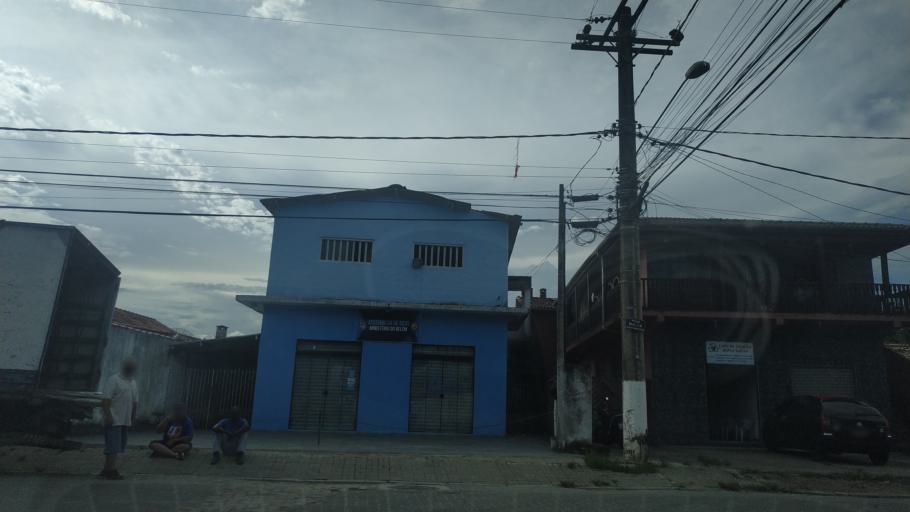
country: BR
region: Sao Paulo
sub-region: Ilhabela
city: Ilhabela
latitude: -23.8238
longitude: -45.3686
